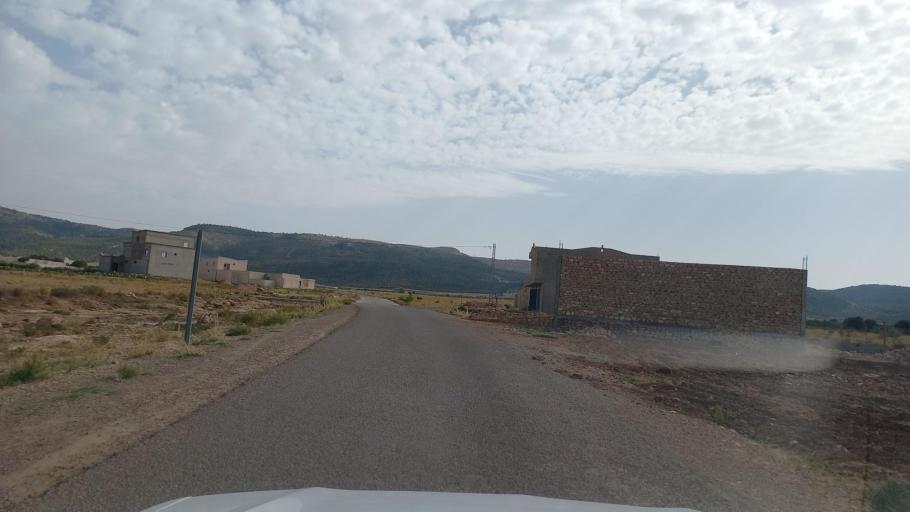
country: TN
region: Al Qasrayn
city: Kasserine
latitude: 35.3552
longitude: 8.8267
